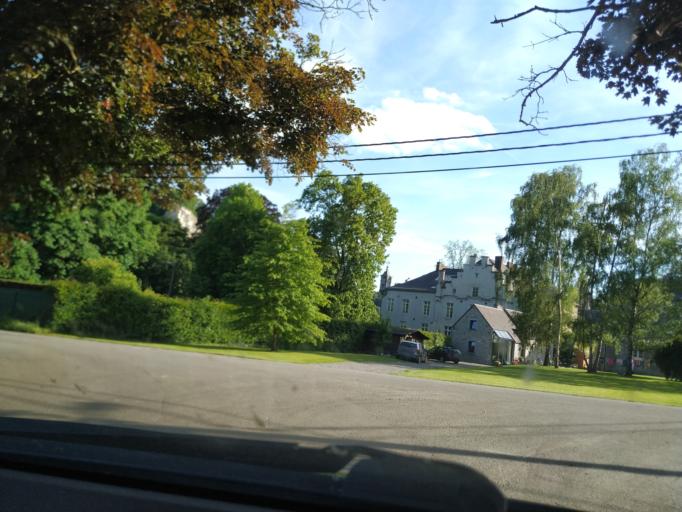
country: BE
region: Wallonia
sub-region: Province de Namur
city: Namur
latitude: 50.4717
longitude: 4.9277
